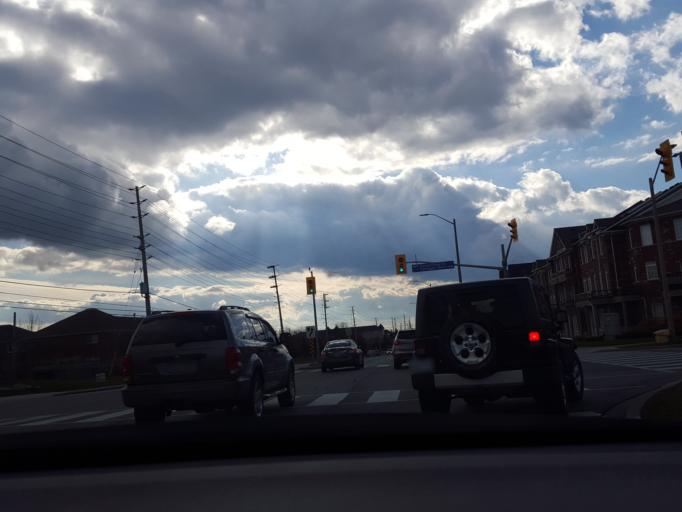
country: CA
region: Ontario
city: Brampton
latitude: 43.5817
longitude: -79.7788
